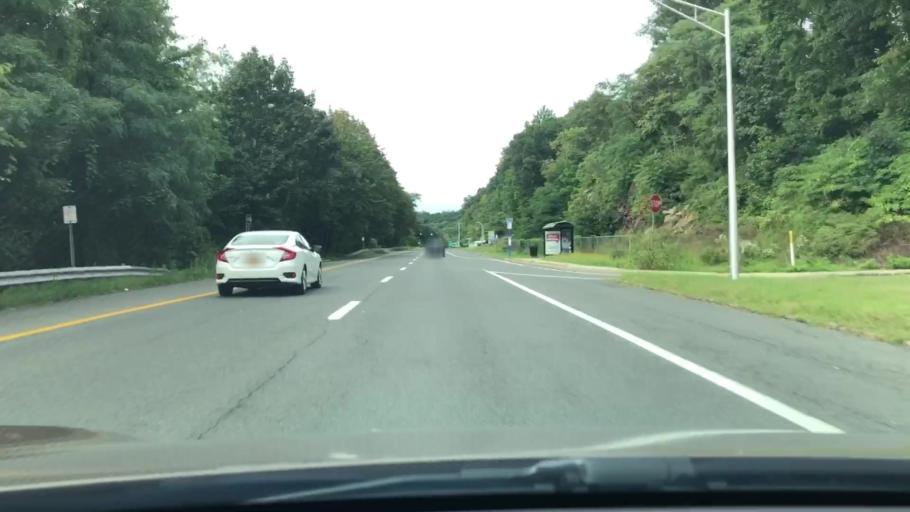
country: US
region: New York
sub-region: Westchester County
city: Purchase
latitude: 41.0186
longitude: -73.7254
